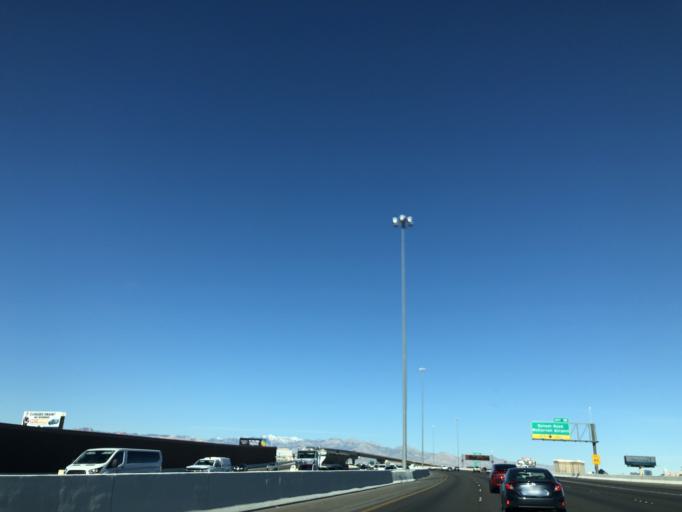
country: US
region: Nevada
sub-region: Clark County
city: Paradise
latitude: 36.0608
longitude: -115.1414
